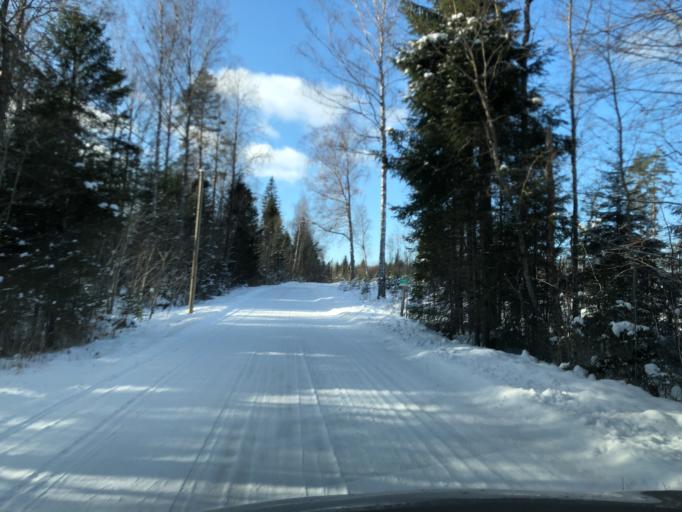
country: EE
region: Jaervamaa
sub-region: Paide linn
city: Paide
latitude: 59.0603
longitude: 25.4951
